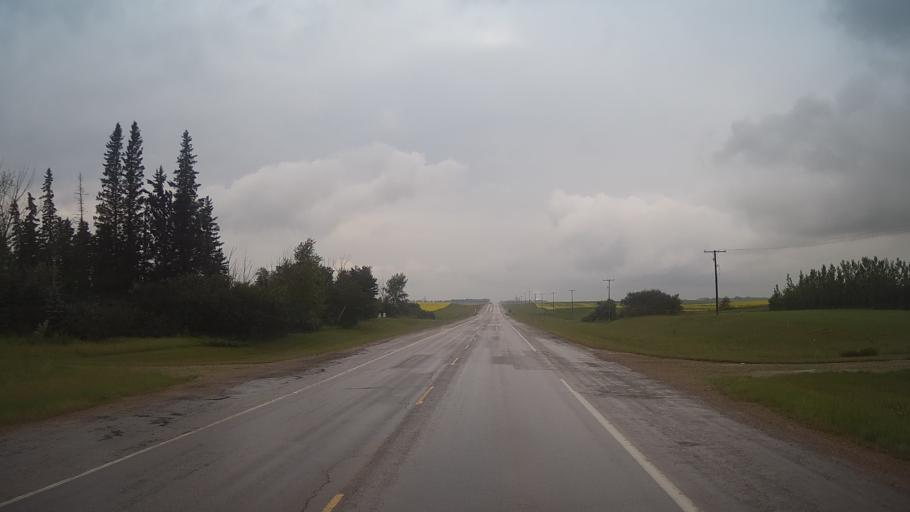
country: CA
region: Saskatchewan
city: Unity
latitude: 52.4350
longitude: -109.0387
